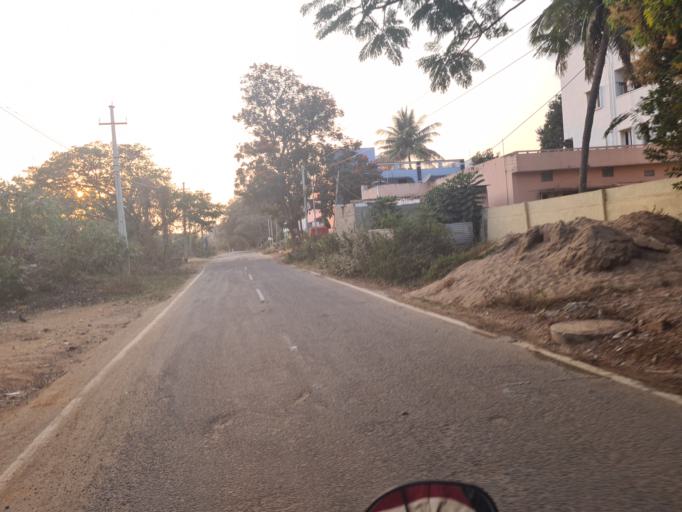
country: IN
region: Telangana
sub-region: Medak
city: Serilingampalle
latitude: 17.4813
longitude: 78.3071
